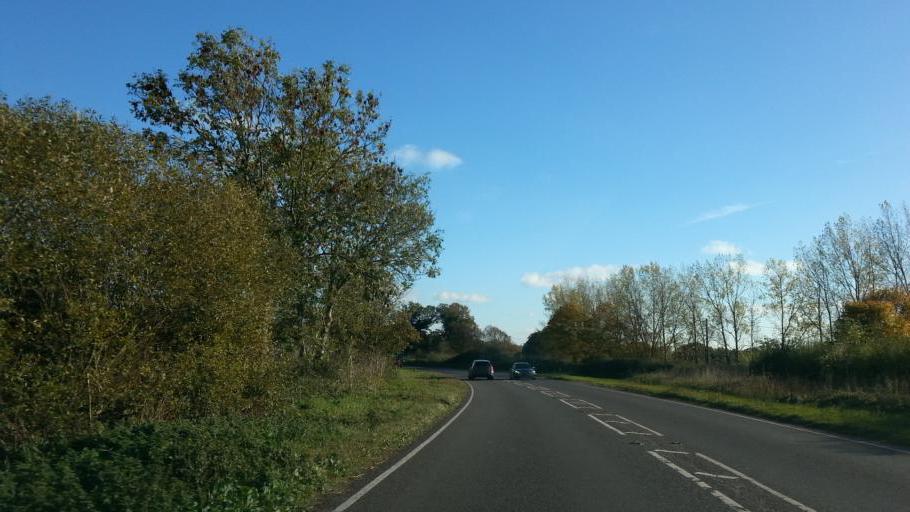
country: GB
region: England
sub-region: Suffolk
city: Beccles
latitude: 52.4768
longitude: 1.5370
